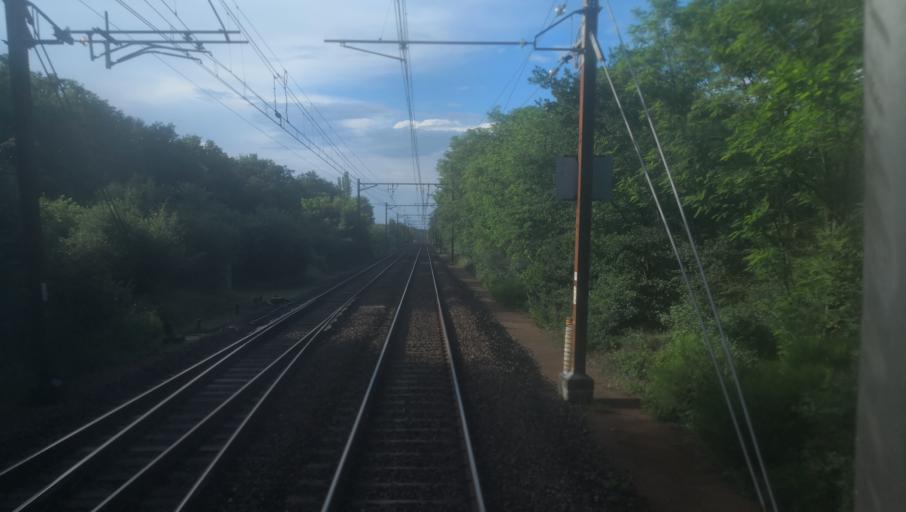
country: FR
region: Centre
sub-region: Departement du Loir-et-Cher
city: Salbris
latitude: 47.4358
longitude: 2.0454
